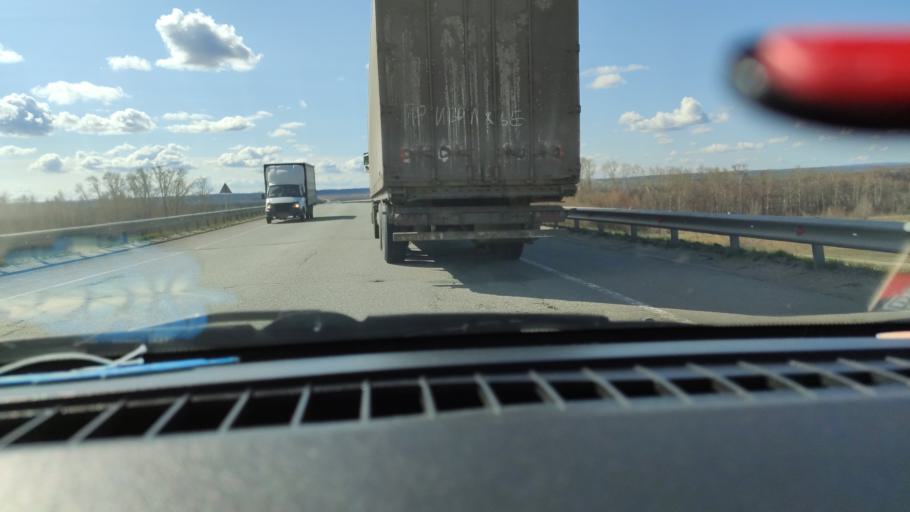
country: RU
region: Samara
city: Varlamovo
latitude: 53.1655
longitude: 48.2815
